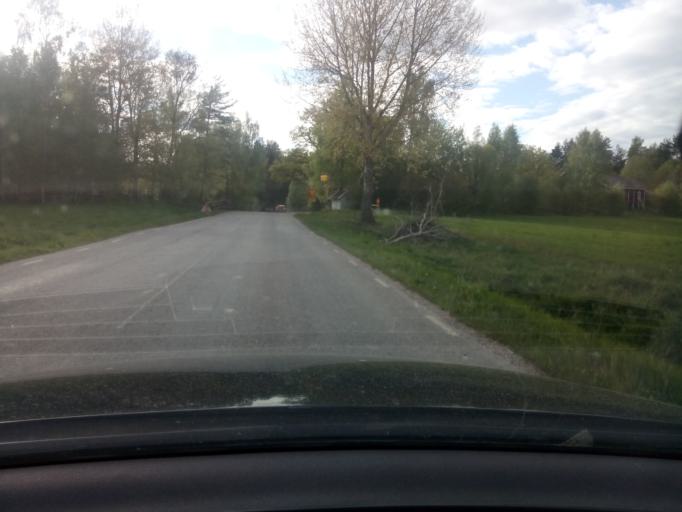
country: SE
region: Soedermanland
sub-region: Nykopings Kommun
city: Stigtomta
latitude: 58.9539
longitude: 16.8599
